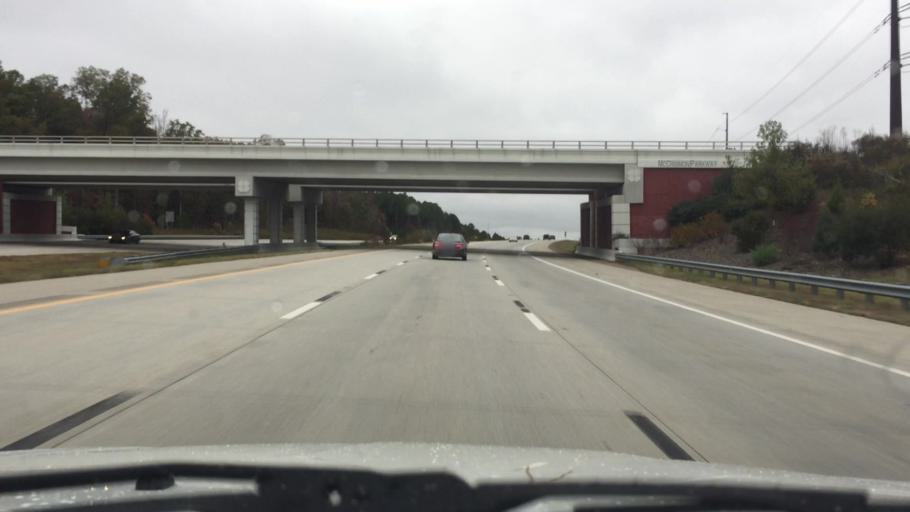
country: US
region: North Carolina
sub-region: Wake County
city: Green Level
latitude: 35.8281
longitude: -78.8933
